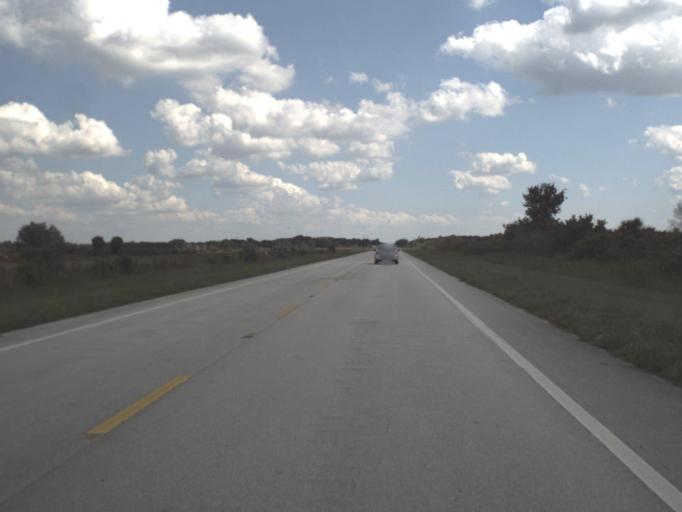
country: US
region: Florida
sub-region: Highlands County
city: Lake Placid
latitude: 27.4093
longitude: -81.1826
